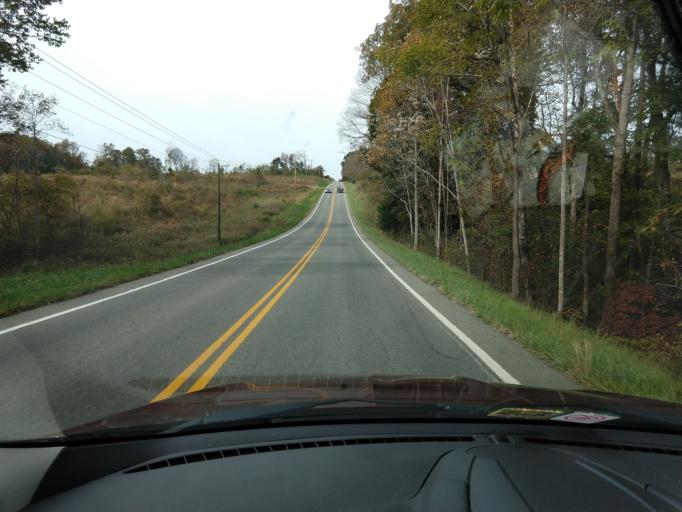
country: US
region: Virginia
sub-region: Franklin County
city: Union Hall
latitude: 36.9891
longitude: -79.6614
